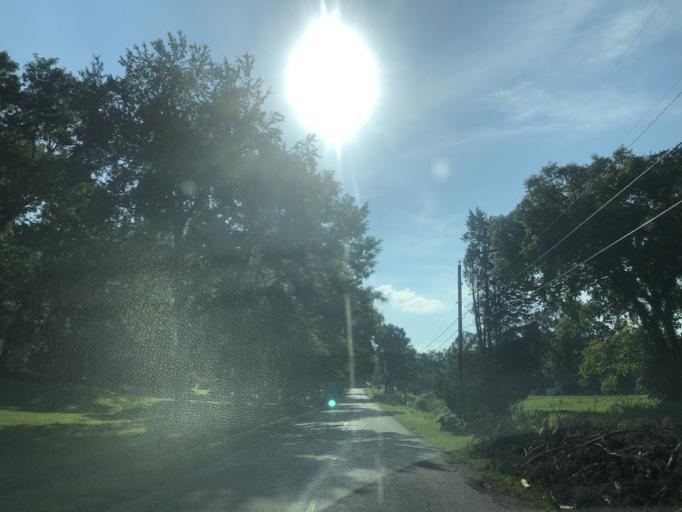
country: US
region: Tennessee
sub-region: Davidson County
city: Nashville
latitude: 36.2382
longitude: -86.8315
